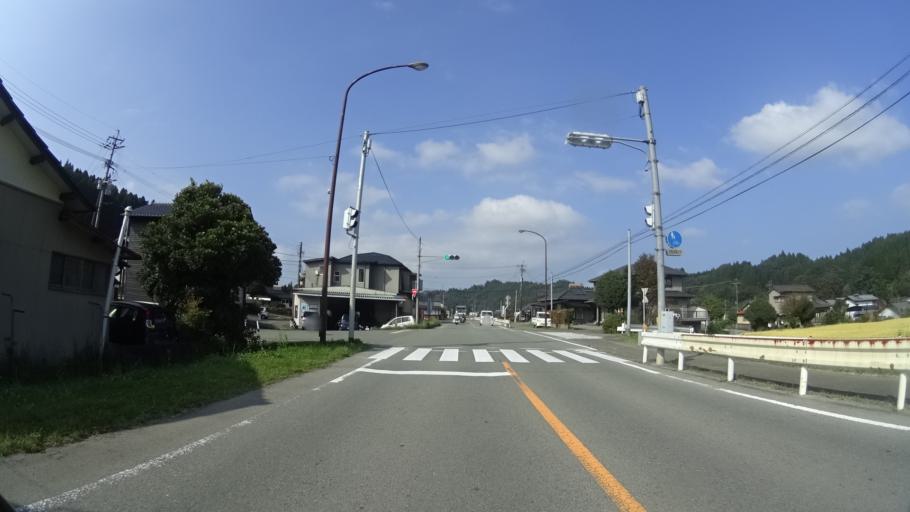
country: JP
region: Kumamoto
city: Aso
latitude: 33.1012
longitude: 131.0679
